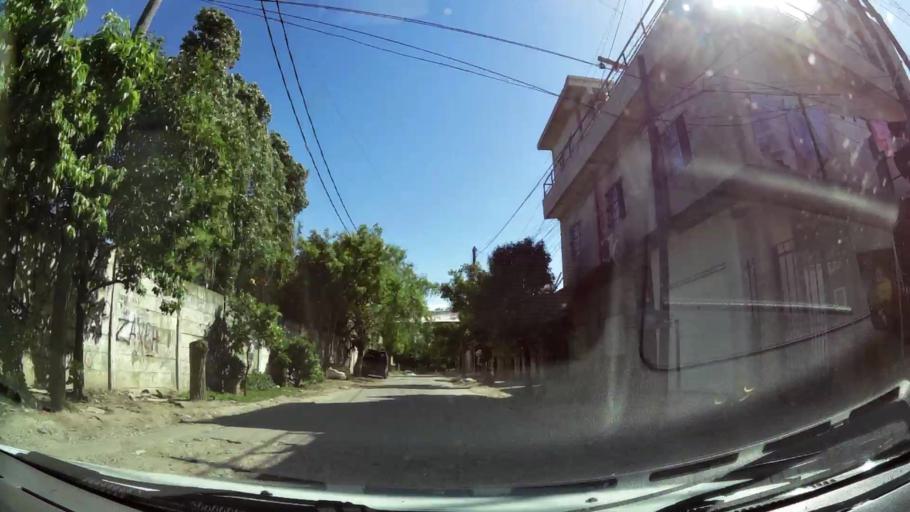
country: AR
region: Buenos Aires
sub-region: Partido de General San Martin
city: General San Martin
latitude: -34.5336
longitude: -58.5799
